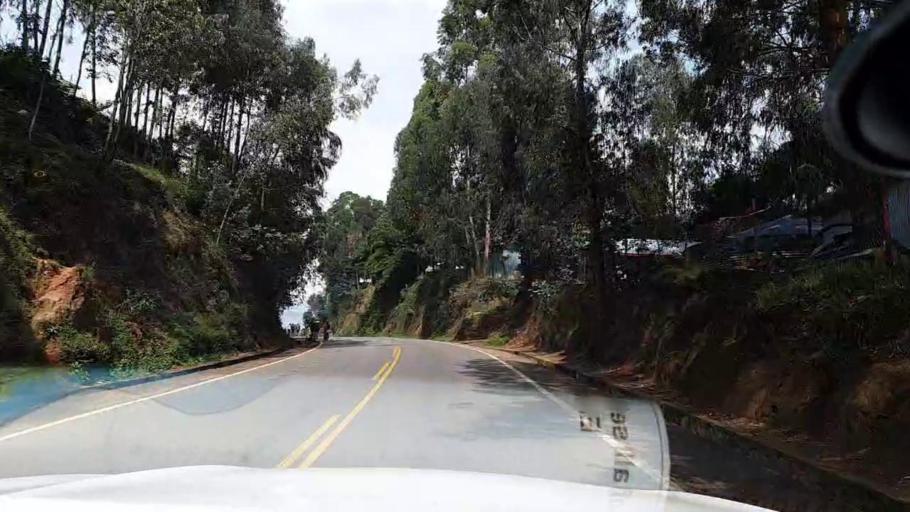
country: RW
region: Southern Province
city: Nzega
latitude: -2.4842
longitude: 29.5242
